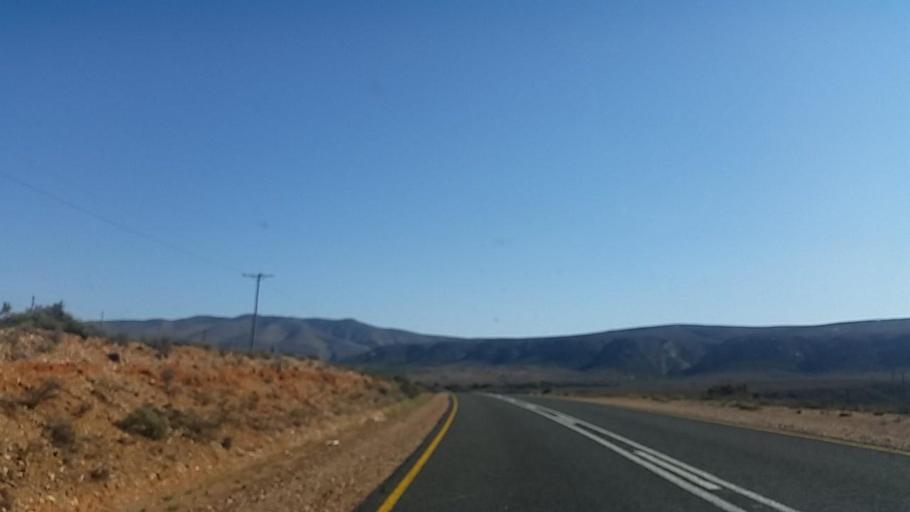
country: ZA
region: Eastern Cape
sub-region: Cacadu District Municipality
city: Willowmore
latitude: -33.4618
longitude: 23.3112
